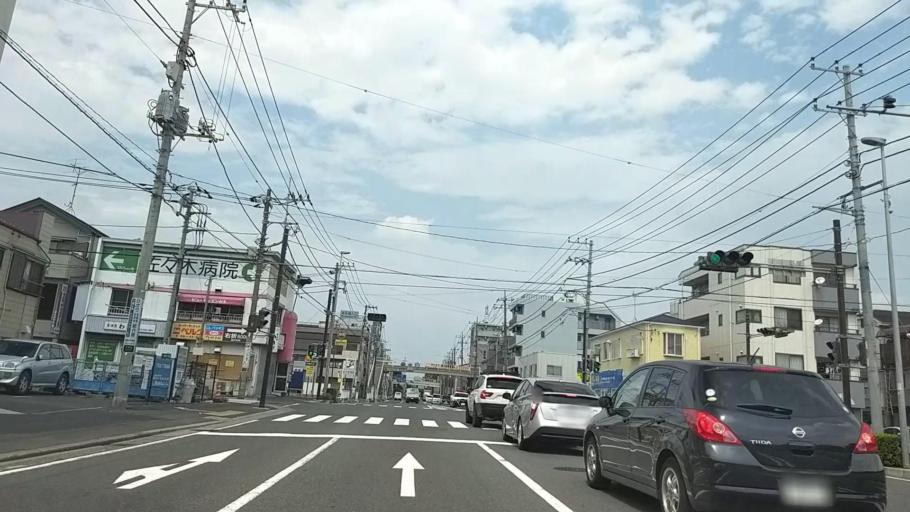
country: JP
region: Kanagawa
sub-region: Kawasaki-shi
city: Kawasaki
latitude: 35.5191
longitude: 139.6727
